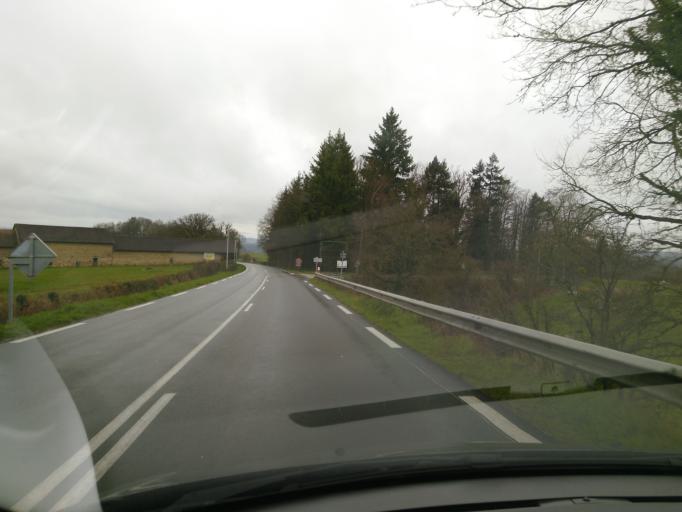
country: FR
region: Limousin
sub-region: Departement de la Haute-Vienne
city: Condat-sur-Vienne
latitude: 45.7713
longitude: 1.2895
